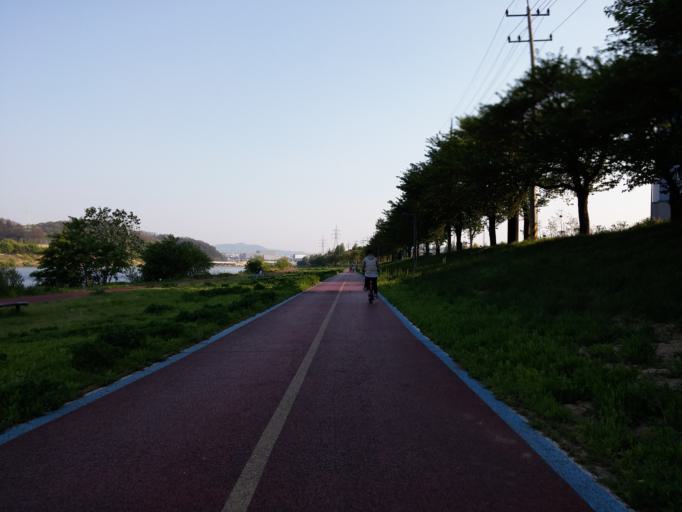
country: KR
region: Daejeon
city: Songgang-dong
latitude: 36.3941
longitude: 127.4101
